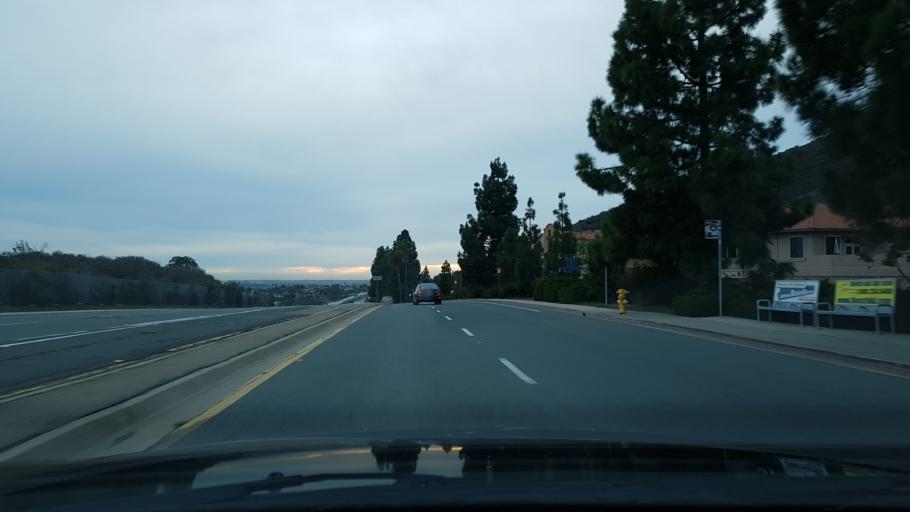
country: US
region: California
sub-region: San Diego County
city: Poway
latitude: 32.9636
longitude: -117.1032
